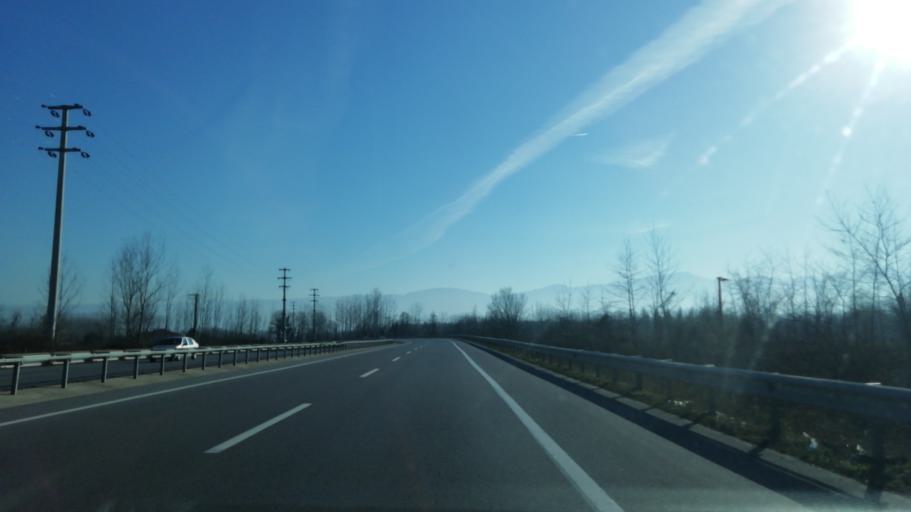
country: TR
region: Sakarya
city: Akyazi
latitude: 40.7008
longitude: 30.5674
